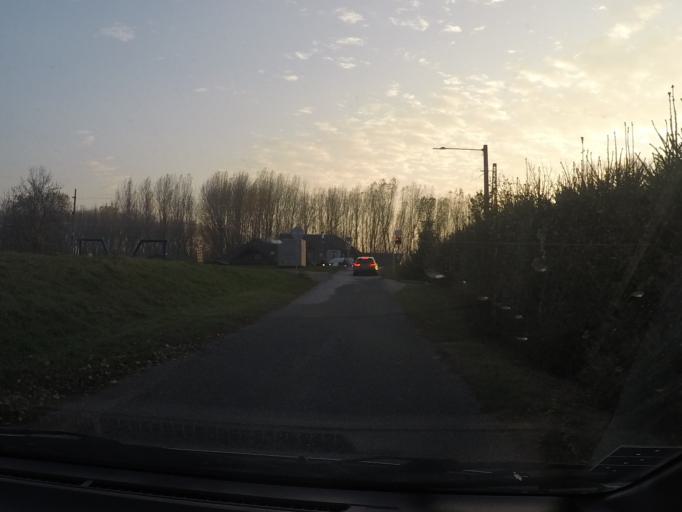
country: SK
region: Nitriansky
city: Levice
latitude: 48.2024
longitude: 18.5254
